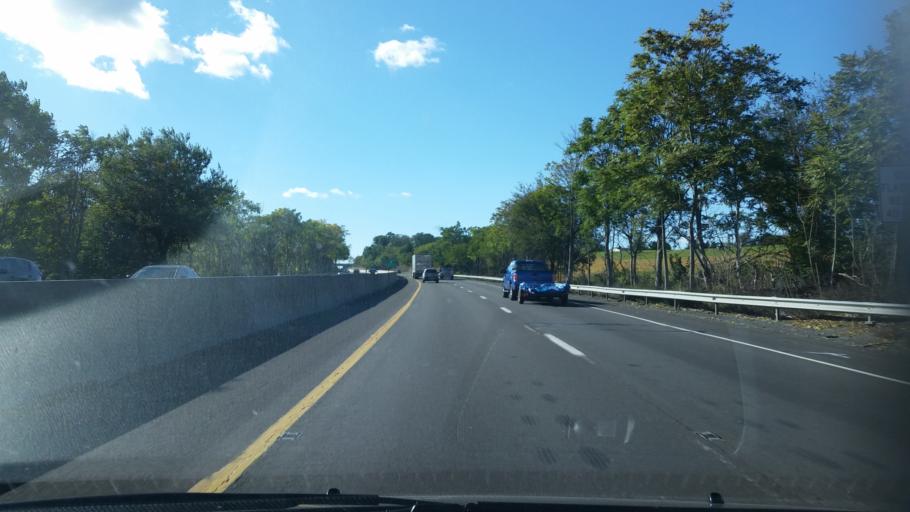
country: US
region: Pennsylvania
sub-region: Lehigh County
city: Breinigsville
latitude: 40.5784
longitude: -75.6806
